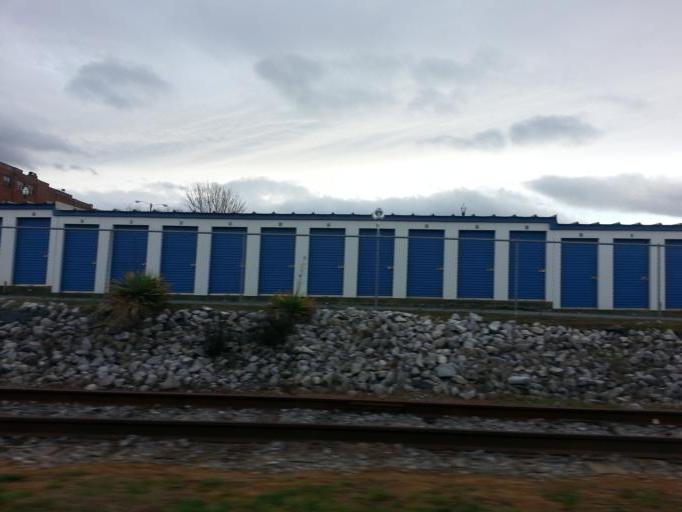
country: US
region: Tennessee
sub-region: Washington County
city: Johnson City
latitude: 36.3153
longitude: -82.3519
